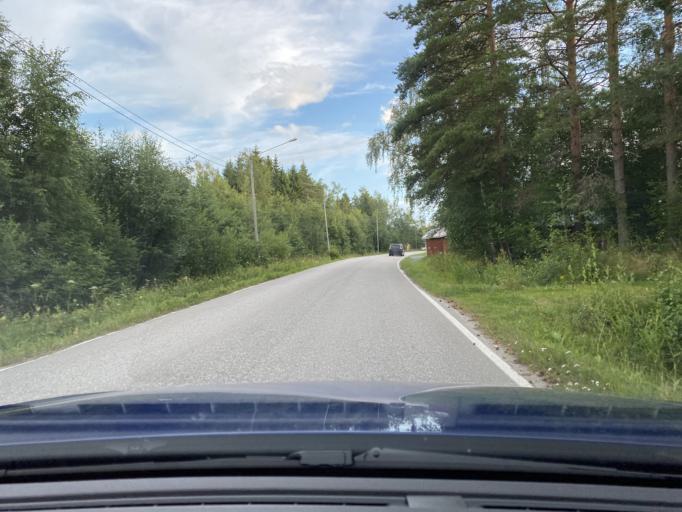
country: FI
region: Ostrobothnia
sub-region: Vaasa
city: Korsnaes
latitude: 62.9594
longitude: 21.1876
